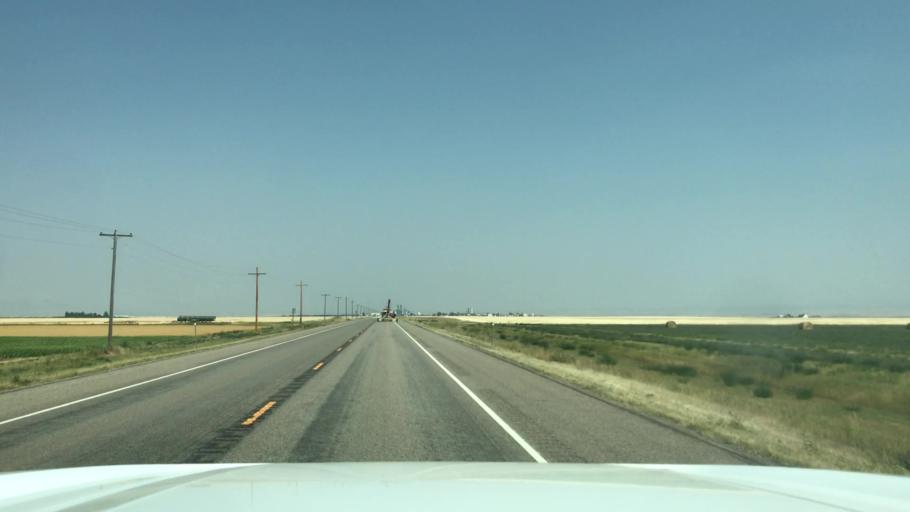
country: US
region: Montana
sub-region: Judith Basin County
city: Stanford
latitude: 47.0552
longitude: -109.9492
